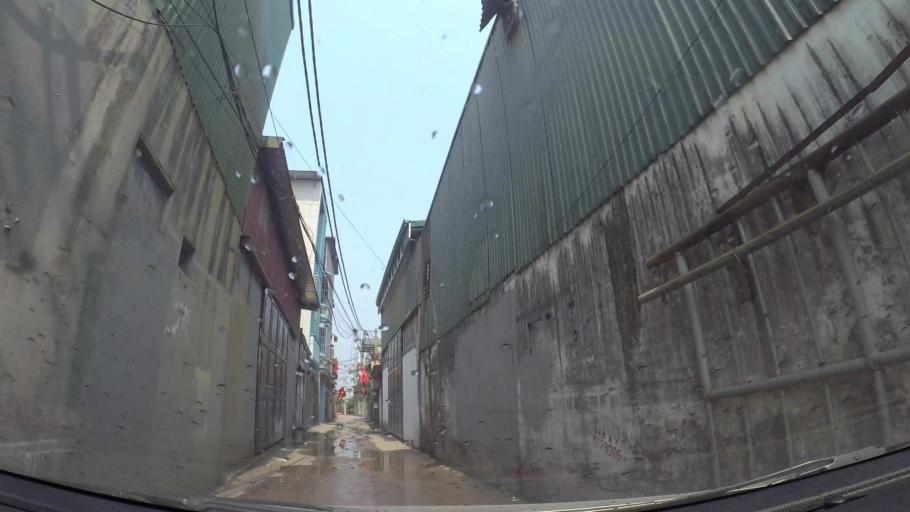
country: VN
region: Ha Noi
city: Cau Dien
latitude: 21.0048
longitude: 105.7589
